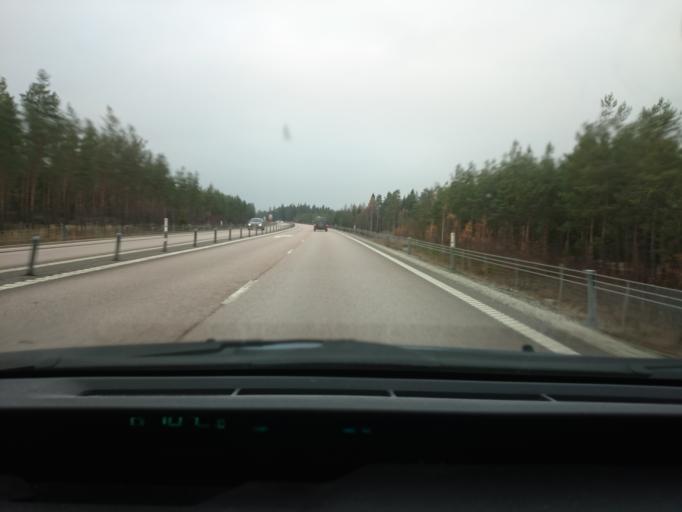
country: SE
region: Vaestmanland
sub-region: Sala Kommun
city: Sala
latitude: 59.9886
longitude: 16.4515
